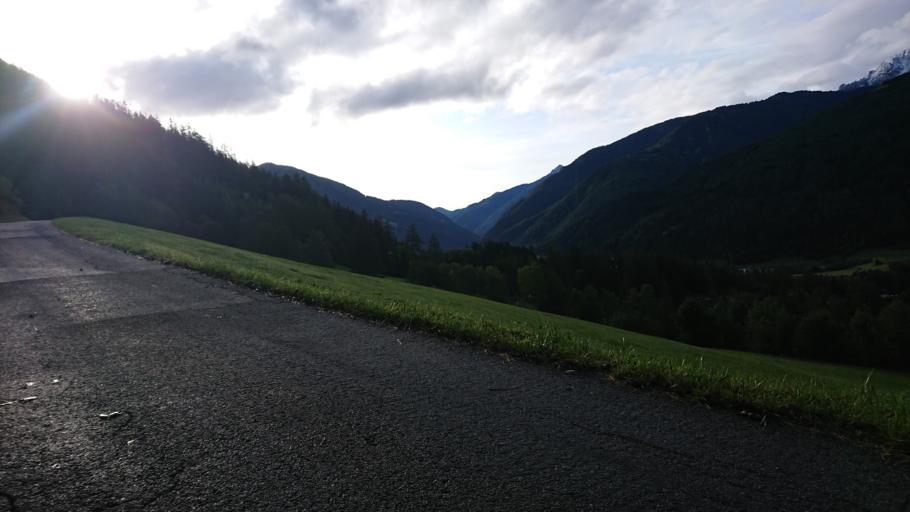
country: IT
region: Trentino-Alto Adige
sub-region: Bolzano
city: Campo di Trens
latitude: 46.8793
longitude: 11.4866
